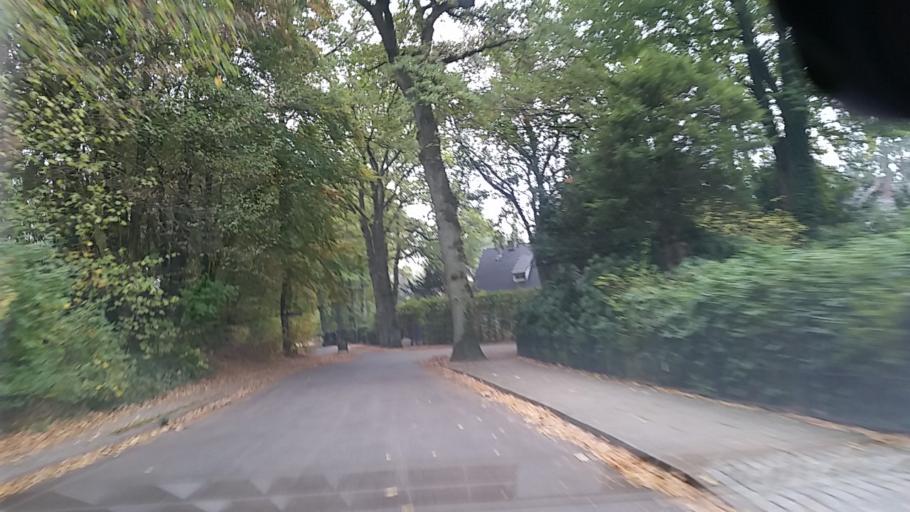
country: DE
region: Schleswig-Holstein
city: Halstenbek
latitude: 53.5712
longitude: 9.8034
